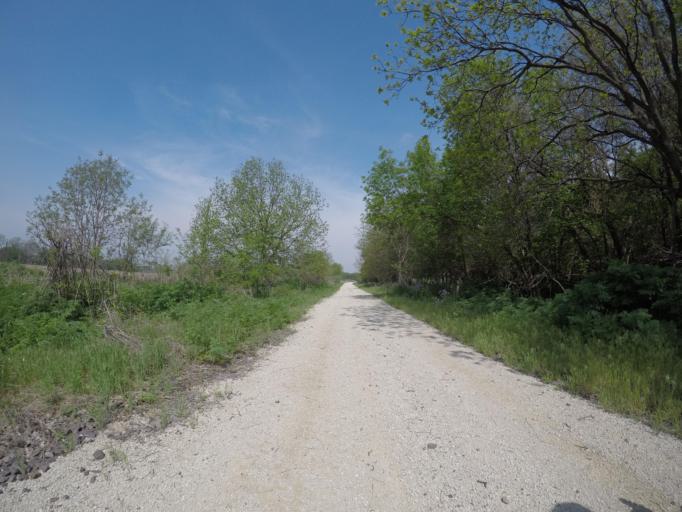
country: US
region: Nebraska
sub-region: Gage County
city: Wymore
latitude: 40.1166
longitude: -96.6319
